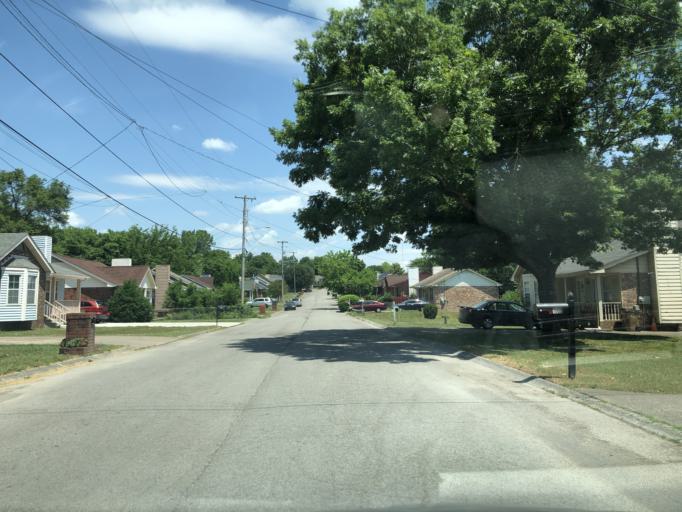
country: US
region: Tennessee
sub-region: Davidson County
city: Goodlettsville
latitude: 36.2680
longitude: -86.7174
